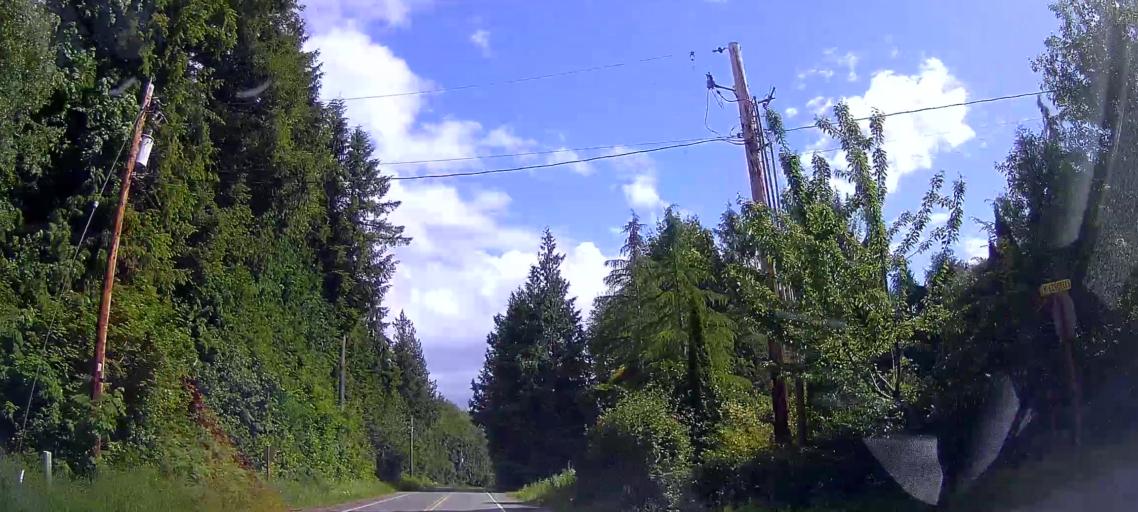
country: US
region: Washington
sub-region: Skagit County
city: Sedro-Woolley
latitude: 48.5565
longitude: -122.2119
